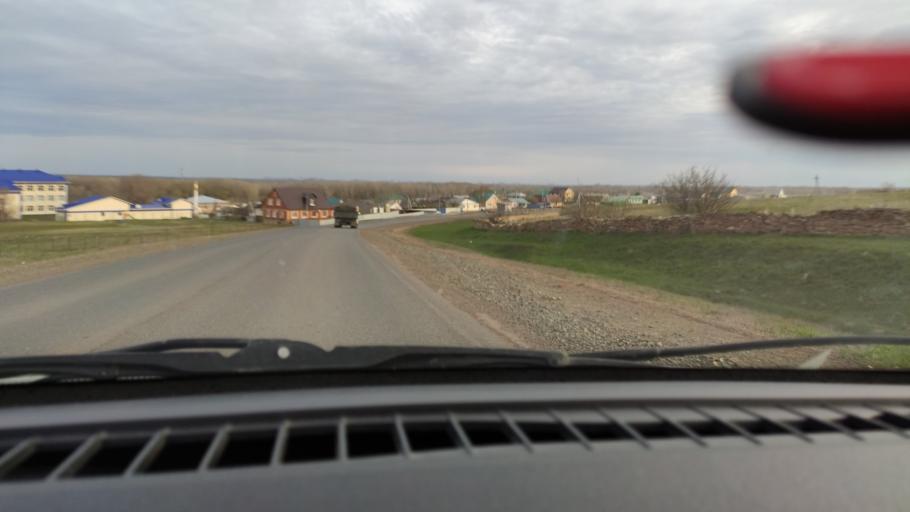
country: RU
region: Orenburg
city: Tatarskaya Kargala
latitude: 51.9503
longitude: 55.1819
